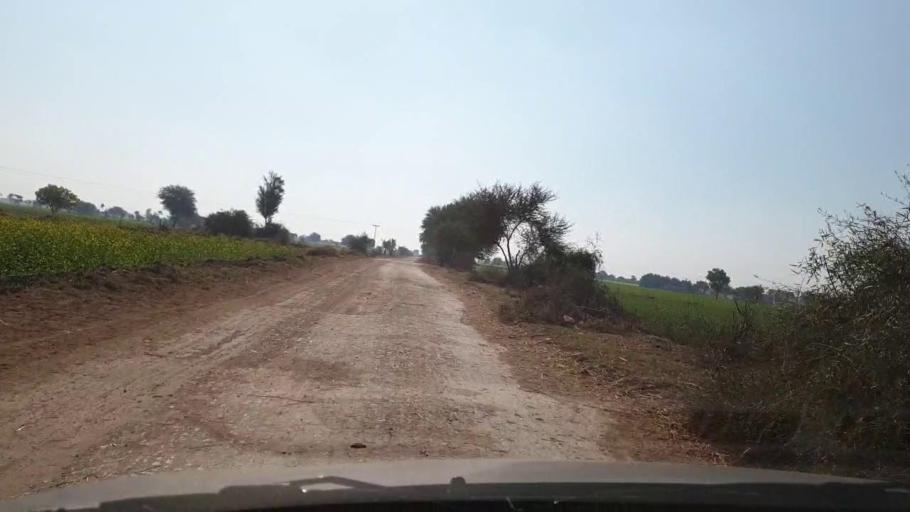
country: PK
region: Sindh
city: Jhol
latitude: 25.9371
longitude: 68.8003
